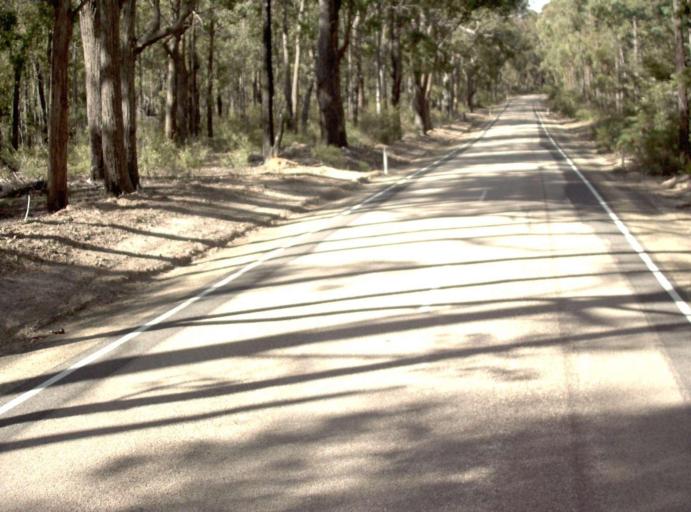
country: AU
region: Victoria
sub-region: East Gippsland
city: Lakes Entrance
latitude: -37.6852
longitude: 148.0503
